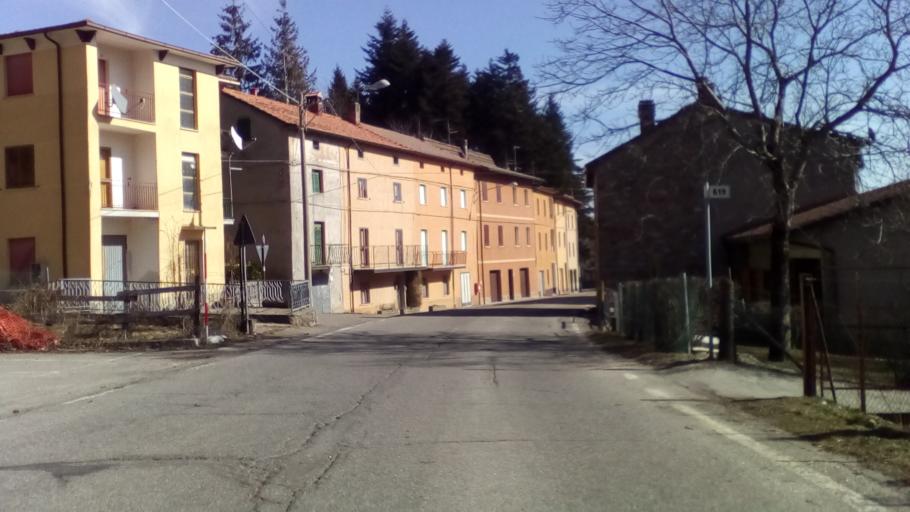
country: IT
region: Emilia-Romagna
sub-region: Provincia di Modena
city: Riolunato
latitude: 44.2718
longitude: 10.6697
